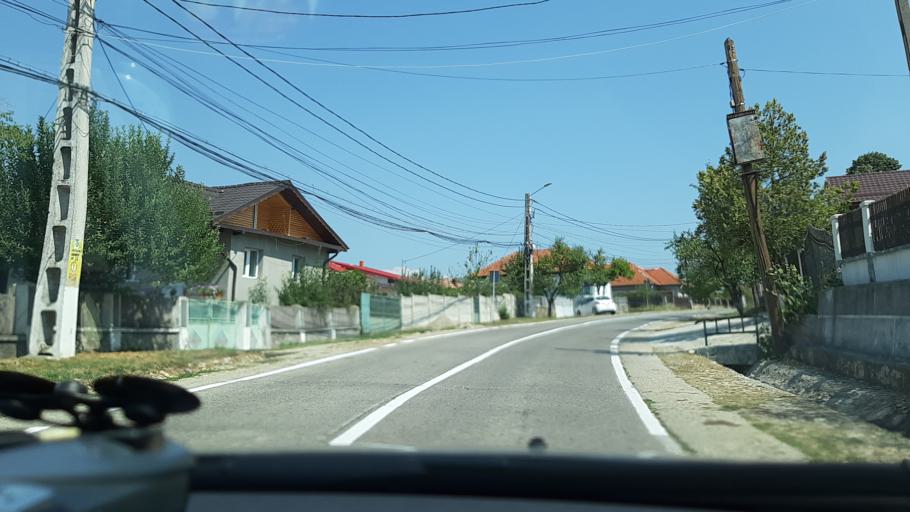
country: RO
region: Gorj
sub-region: Comuna Targu Carbunesti
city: Targu Carbunesti
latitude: 44.9451
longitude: 23.5370
